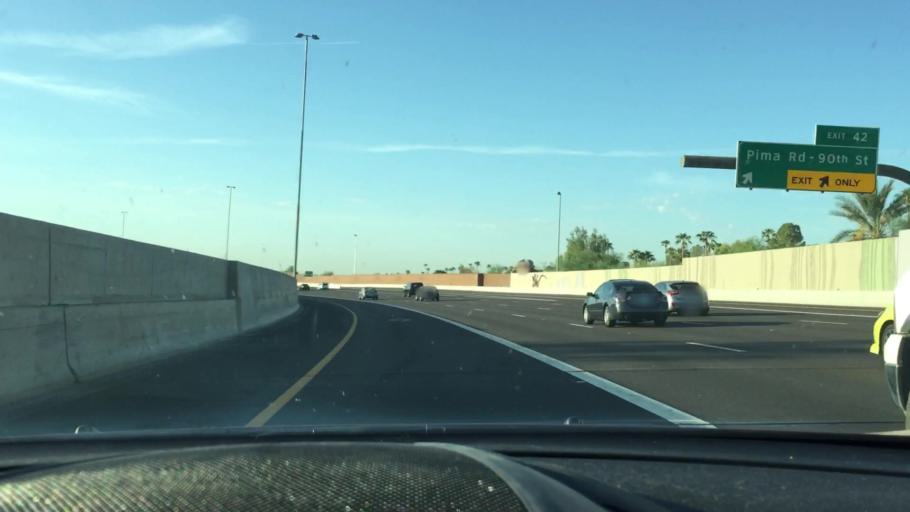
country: US
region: Arizona
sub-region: Maricopa County
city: Scottsdale
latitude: 33.5689
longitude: -111.8915
